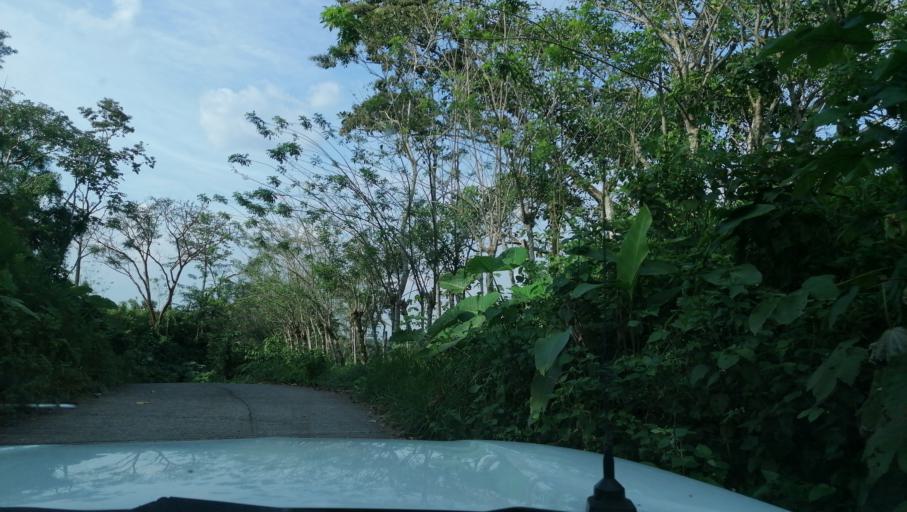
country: MX
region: Chiapas
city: Ostuacan
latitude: 17.4798
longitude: -93.2392
